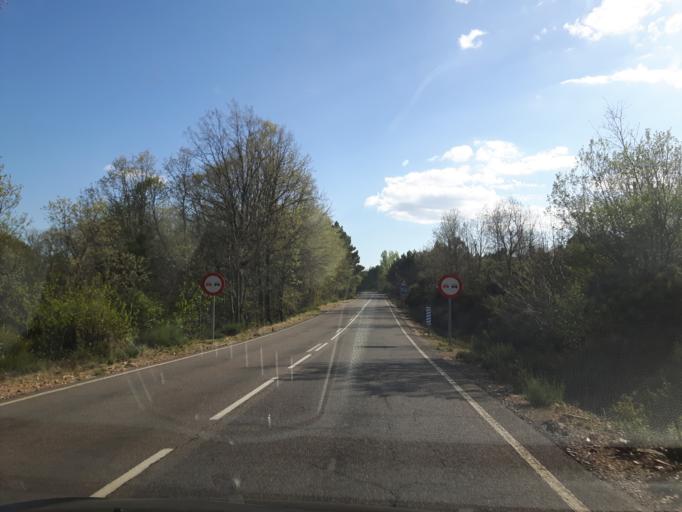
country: ES
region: Castille and Leon
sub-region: Provincia de Salamanca
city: San Miguel de Valero
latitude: 40.5592
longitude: -5.9123
